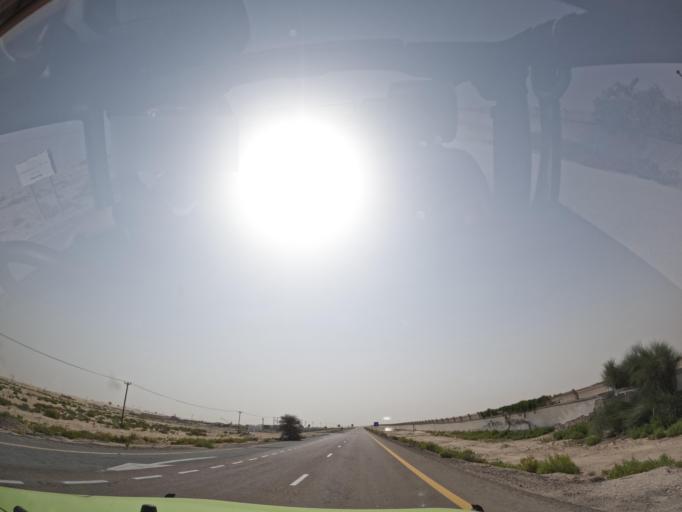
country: AE
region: Dubai
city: Dubai
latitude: 24.6671
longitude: 55.1746
